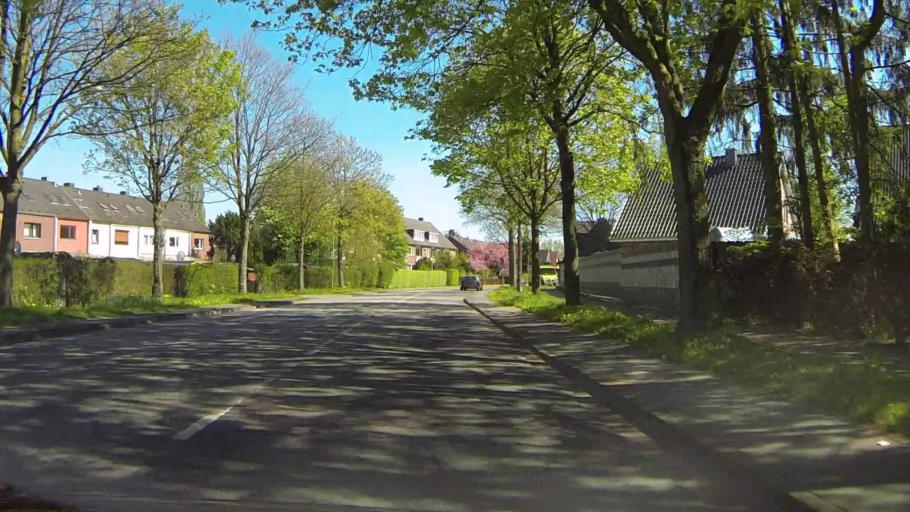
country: DE
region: Schleswig-Holstein
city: Pinneberg
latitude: 53.6682
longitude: 9.7853
